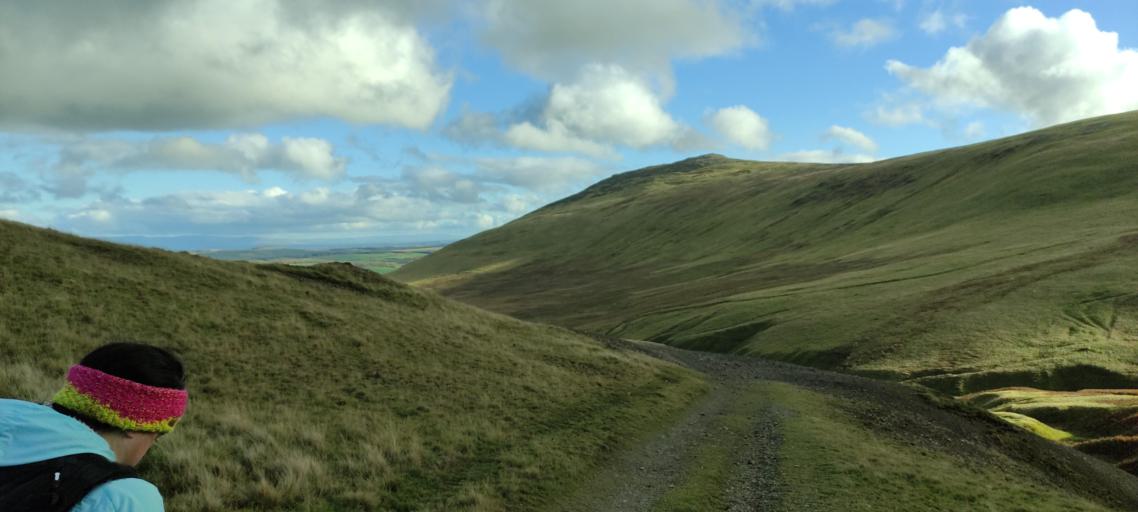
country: GB
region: England
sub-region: Cumbria
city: Keswick
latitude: 54.7077
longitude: -3.0442
